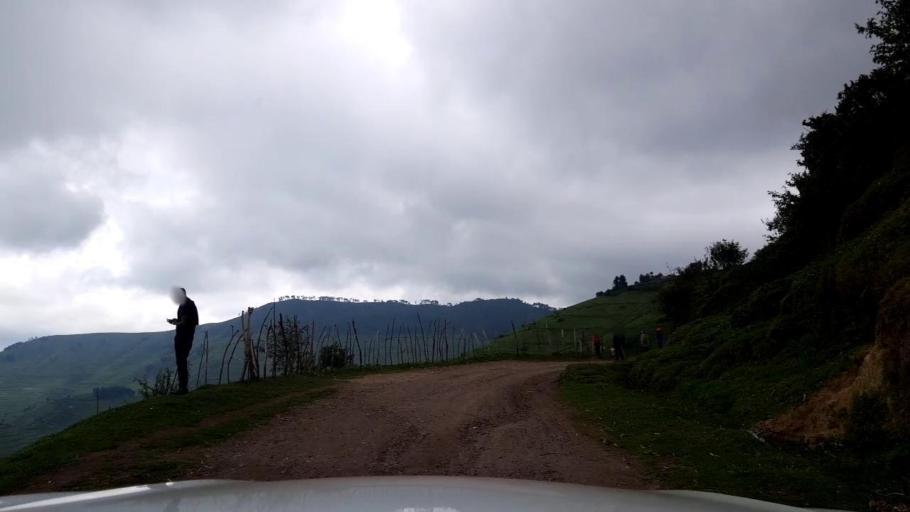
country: RW
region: Western Province
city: Gisenyi
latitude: -1.6725
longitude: 29.4112
